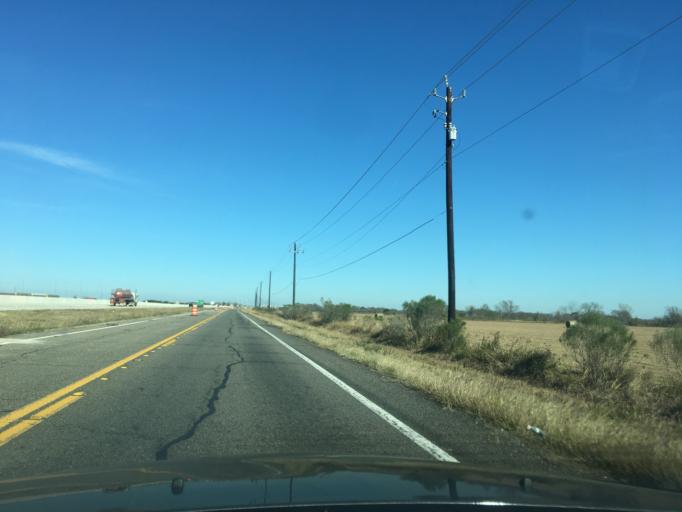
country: US
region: Texas
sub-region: Wharton County
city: East Bernard
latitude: 29.4585
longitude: -95.9796
